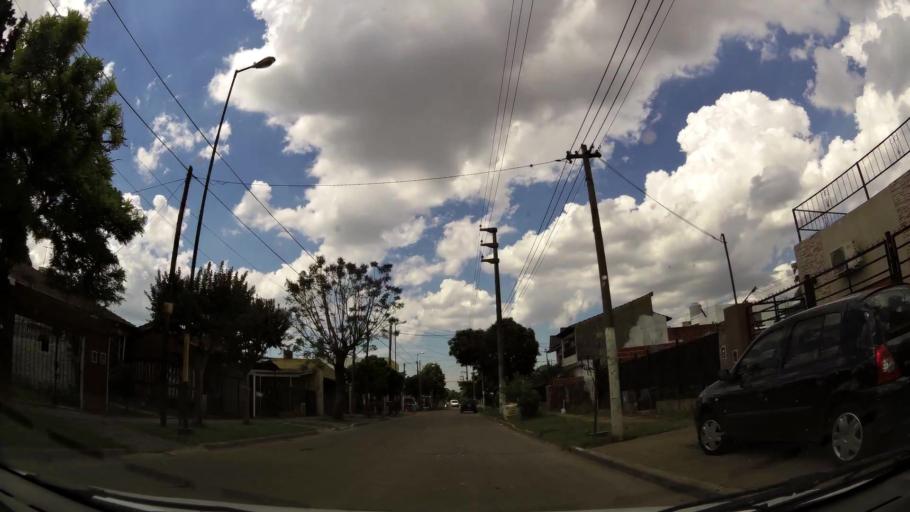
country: AR
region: Buenos Aires
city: Ituzaingo
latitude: -34.6424
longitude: -58.6759
